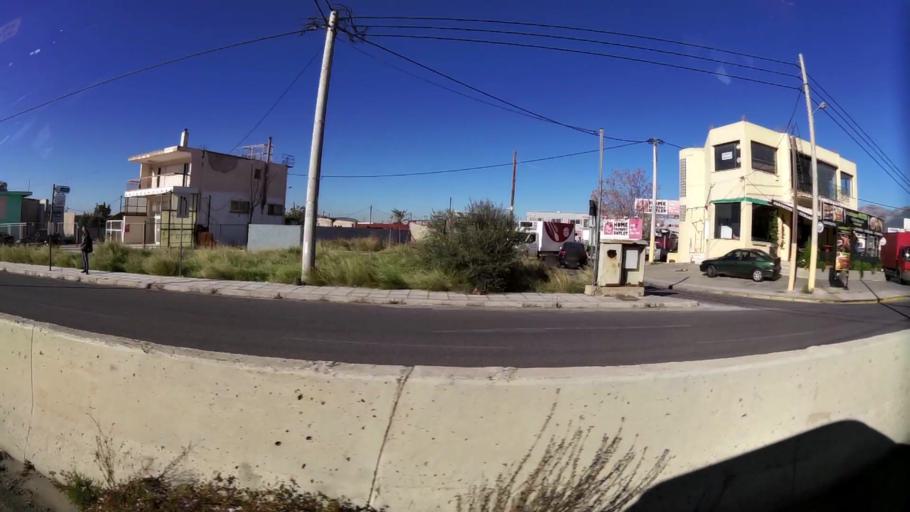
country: GR
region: Attica
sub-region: Nomarchia Athinas
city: Metamorfosi
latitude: 38.0850
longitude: 23.7638
